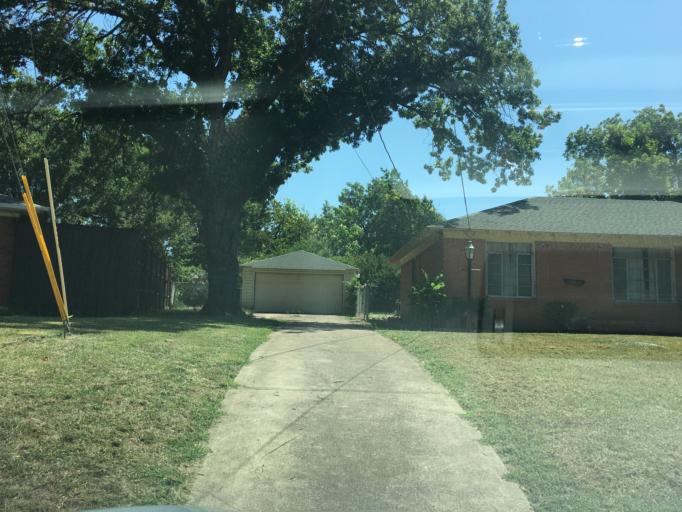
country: US
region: Texas
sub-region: Dallas County
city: Highland Park
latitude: 32.8504
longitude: -96.7478
